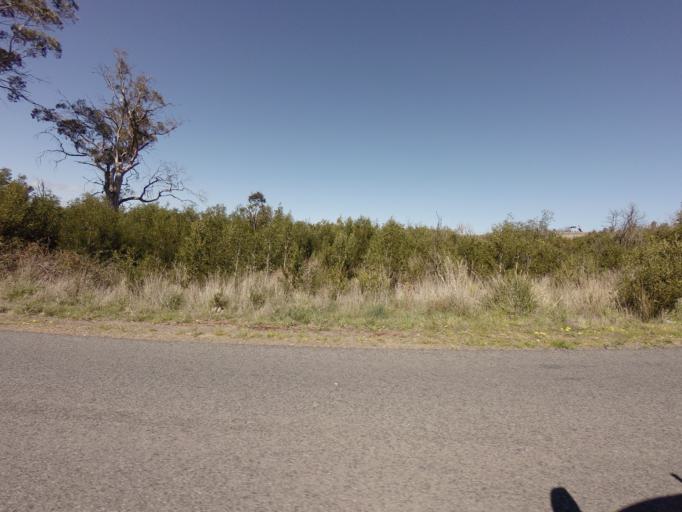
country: AU
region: Tasmania
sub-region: Derwent Valley
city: New Norfolk
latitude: -42.5389
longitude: 146.7215
